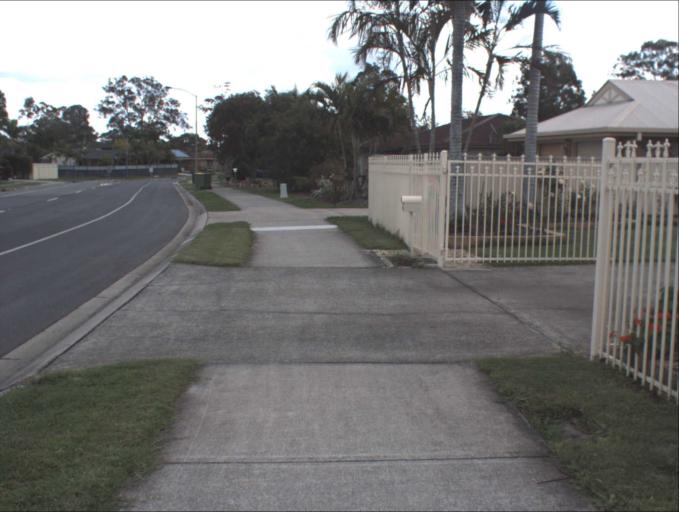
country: AU
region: Queensland
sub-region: Logan
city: Waterford West
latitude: -27.6896
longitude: 153.1546
